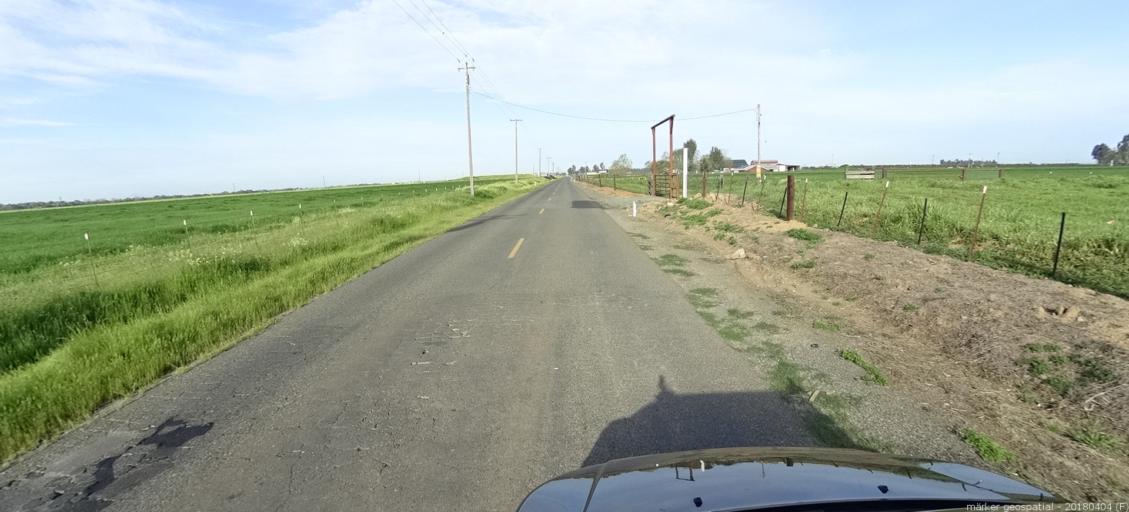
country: US
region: California
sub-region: Sacramento County
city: Herald
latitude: 38.3257
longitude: -121.2631
